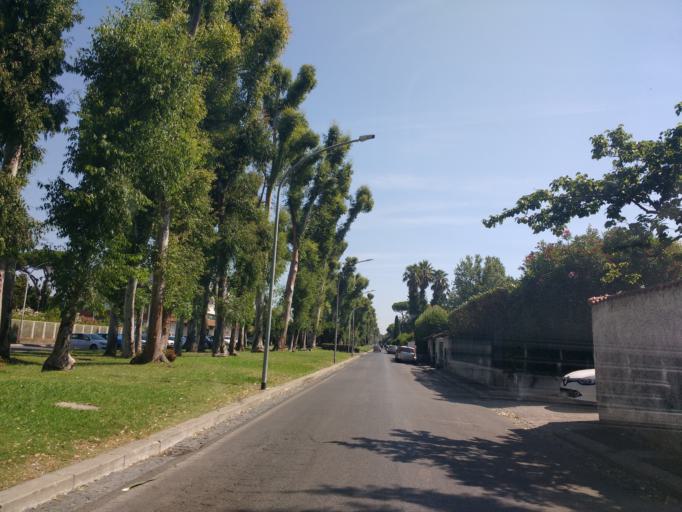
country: IT
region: Latium
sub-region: Citta metropolitana di Roma Capitale
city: Acilia-Castel Fusano-Ostia Antica
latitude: 41.7521
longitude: 12.3574
